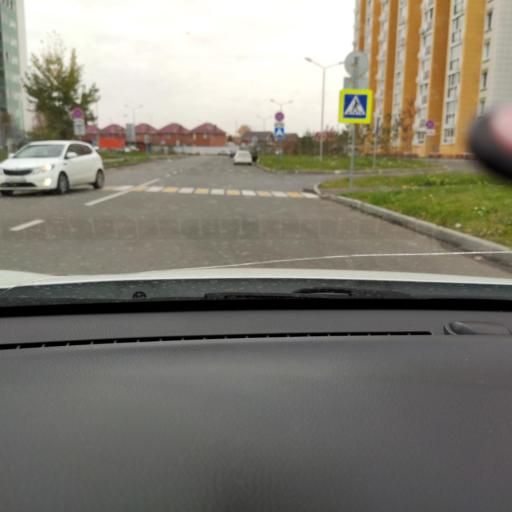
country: RU
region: Tatarstan
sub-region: Gorod Kazan'
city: Kazan
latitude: 55.7955
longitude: 49.2492
